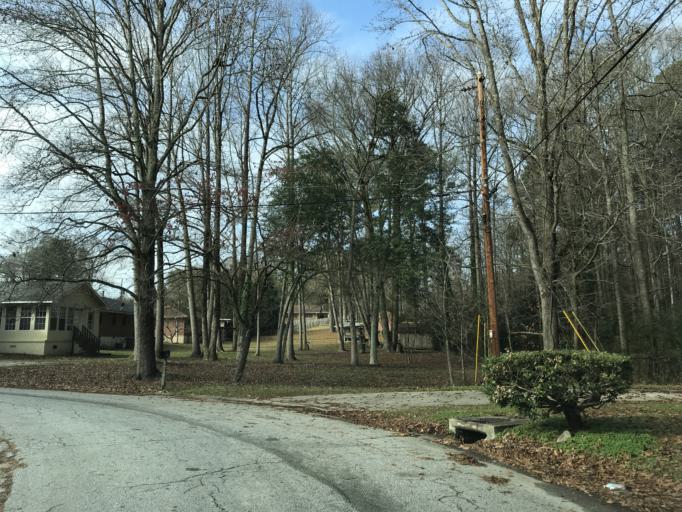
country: US
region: Georgia
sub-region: Clayton County
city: Morrow
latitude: 33.5602
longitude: -84.3641
